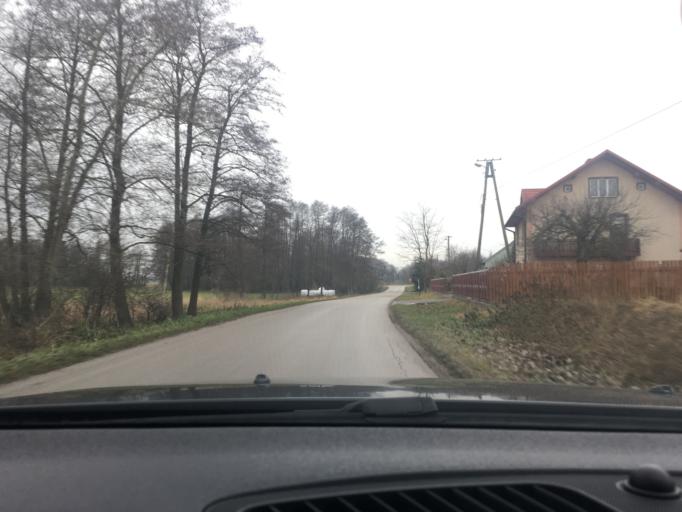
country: PL
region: Swietokrzyskie
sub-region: Powiat jedrzejowski
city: Imielno
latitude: 50.6423
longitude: 20.4007
